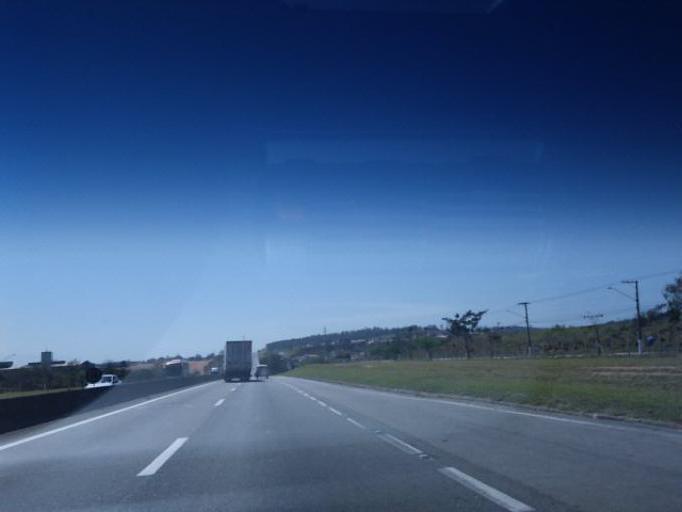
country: BR
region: Sao Paulo
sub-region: Cacapava
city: Cacapava
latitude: -23.1039
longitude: -45.6937
